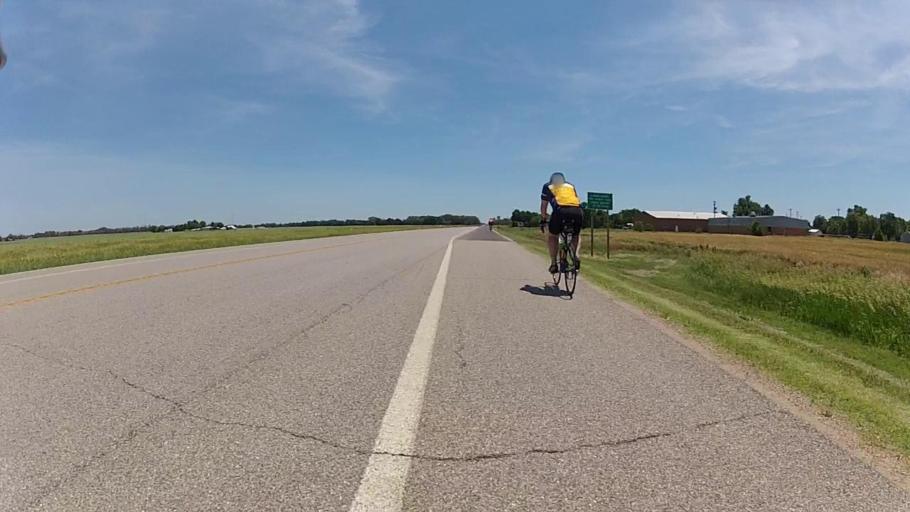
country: US
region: Kansas
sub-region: Barber County
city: Medicine Lodge
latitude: 37.2536
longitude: -98.4217
